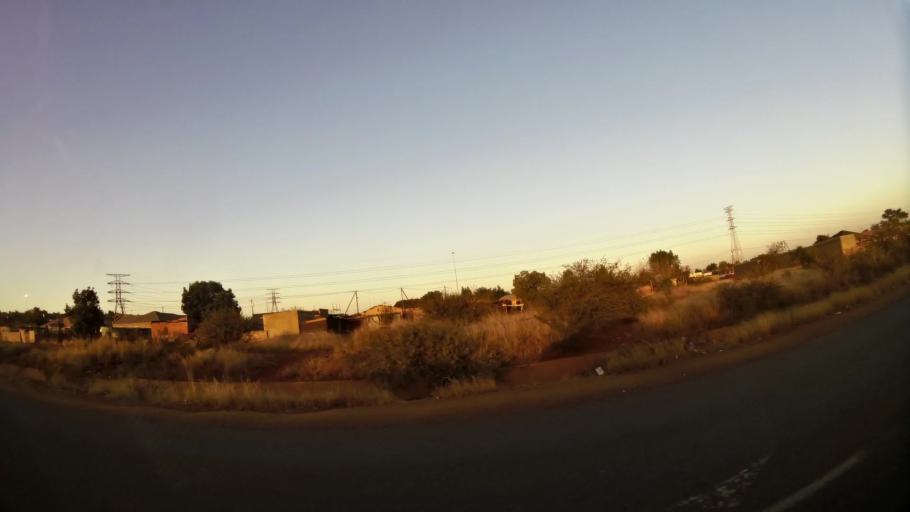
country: ZA
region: Gauteng
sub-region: City of Tshwane Metropolitan Municipality
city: Mabopane
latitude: -25.5782
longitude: 28.0745
